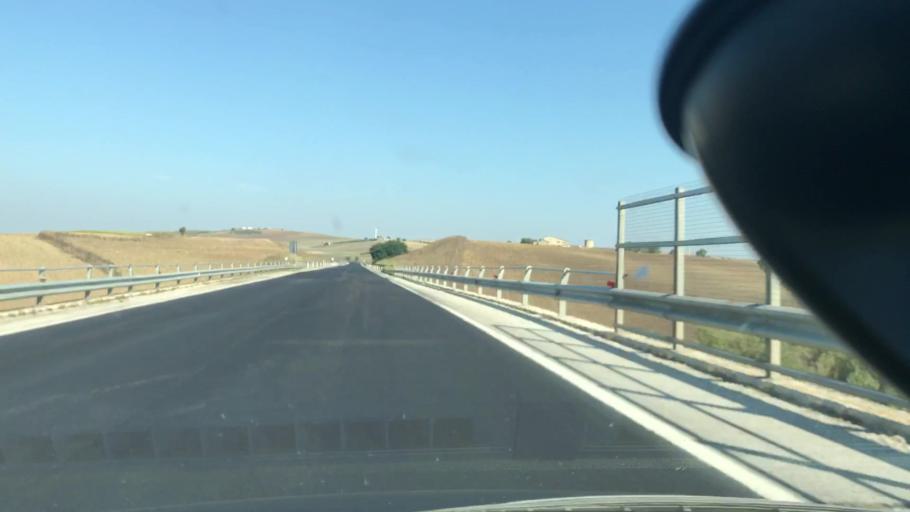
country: IT
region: Apulia
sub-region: Provincia di Barletta - Andria - Trani
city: Spinazzola
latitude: 40.9127
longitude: 16.1053
